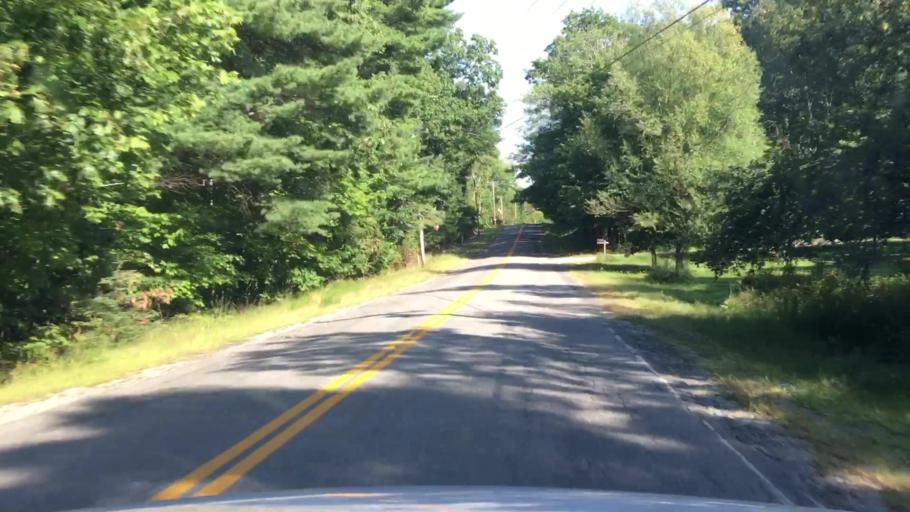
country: US
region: Maine
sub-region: Penobscot County
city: Enfield
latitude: 45.2397
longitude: -68.5575
